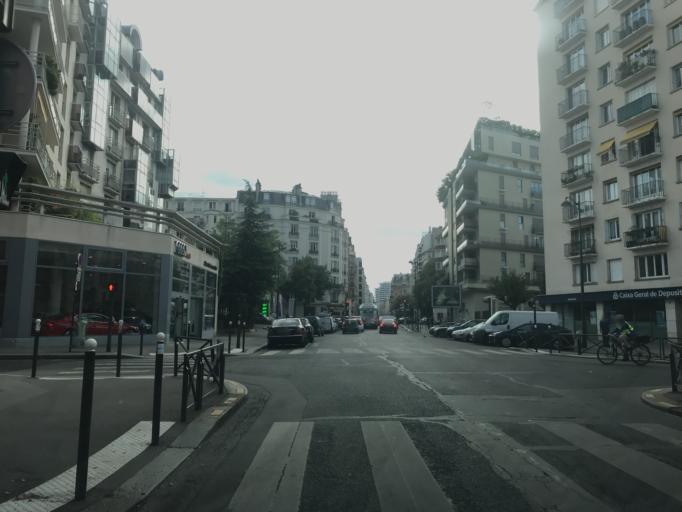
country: FR
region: Ile-de-France
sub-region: Departement des Hauts-de-Seine
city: Vanves
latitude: 48.8397
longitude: 2.2932
